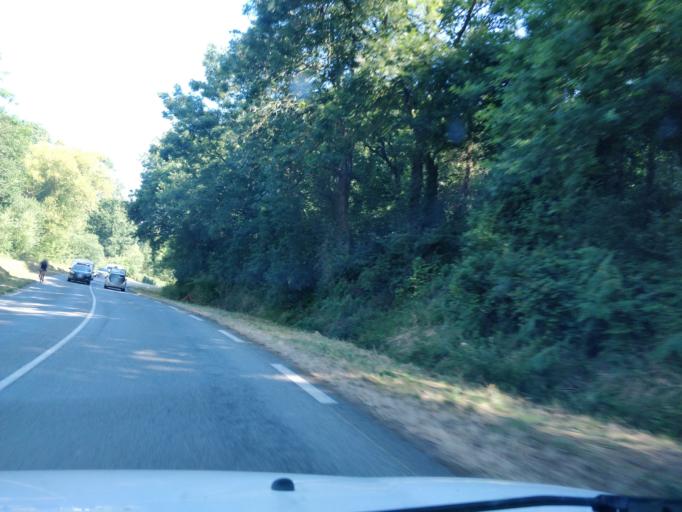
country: FR
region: Brittany
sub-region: Departement des Cotes-d'Armor
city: Binic
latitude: 48.5884
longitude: -2.8257
